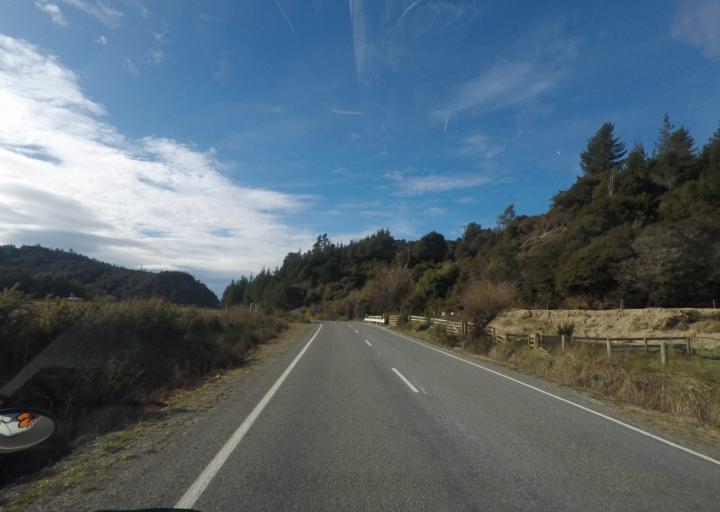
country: NZ
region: Tasman
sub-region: Tasman District
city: Motueka
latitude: -41.0169
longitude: 172.9836
